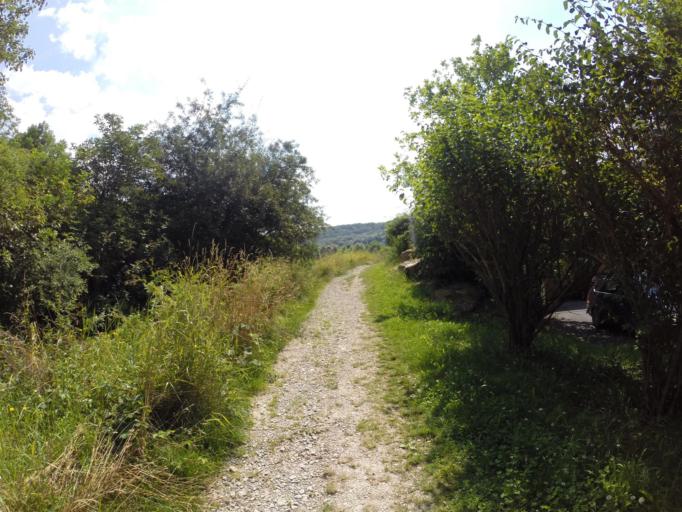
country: DE
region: Thuringia
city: Jena
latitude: 50.9313
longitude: 11.6264
